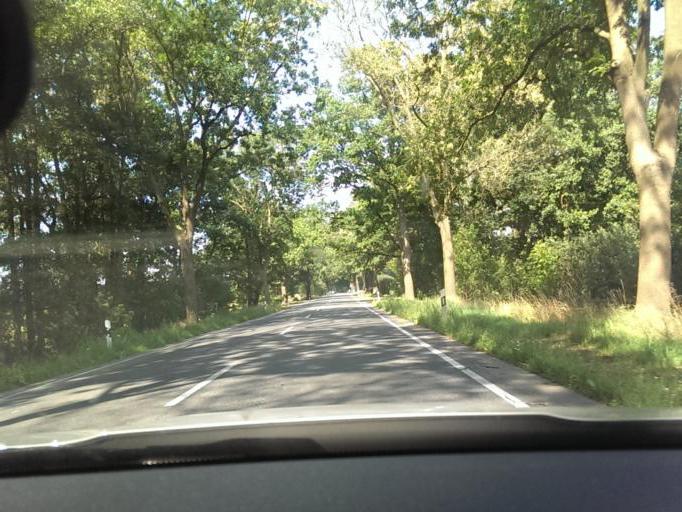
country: DE
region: Lower Saxony
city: Langenhagen
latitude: 52.5024
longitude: 9.7278
